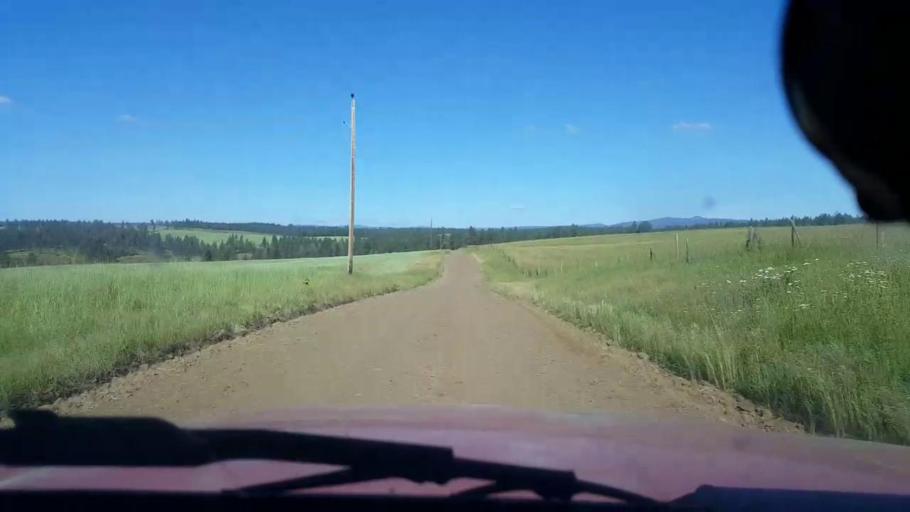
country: US
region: Washington
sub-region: Garfield County
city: Pomeroy
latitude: 45.9845
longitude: -117.4635
